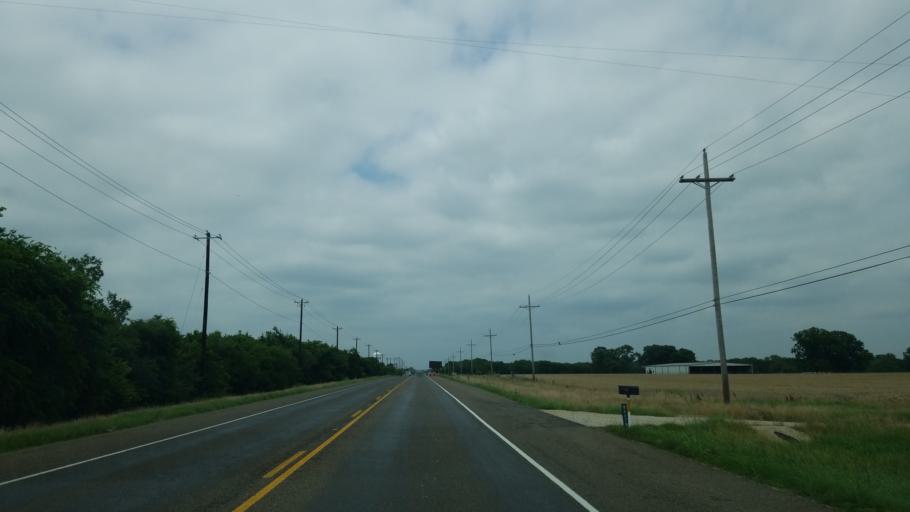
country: US
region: Texas
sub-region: Denton County
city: Pilot Point
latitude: 33.3609
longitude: -96.9656
